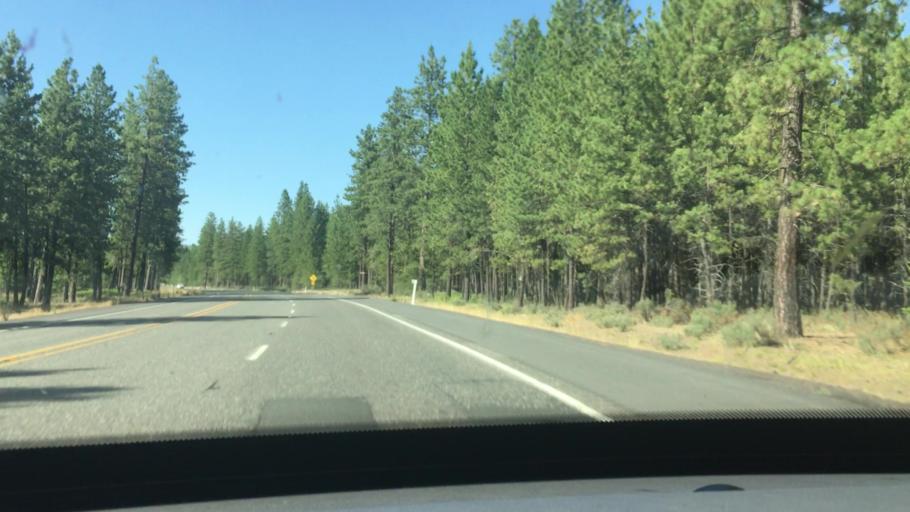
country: US
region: Washington
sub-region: Klickitat County
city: Goldendale
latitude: 45.9238
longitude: -120.6994
